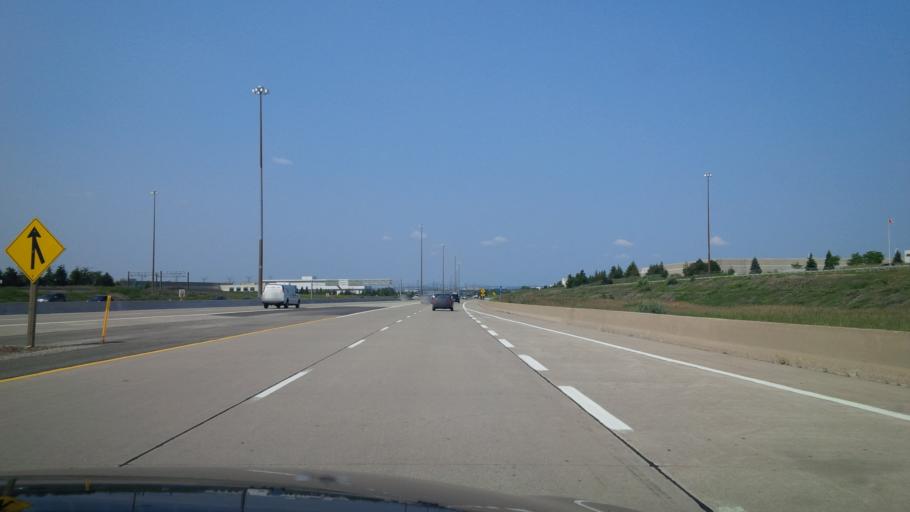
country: CA
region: Ontario
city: Concord
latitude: 43.7815
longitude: -79.5466
